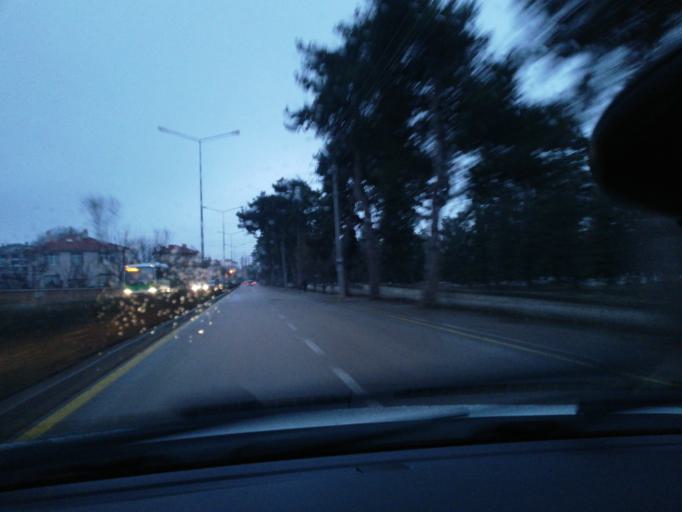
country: TR
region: Bolu
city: Bolu
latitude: 40.7302
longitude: 31.5806
